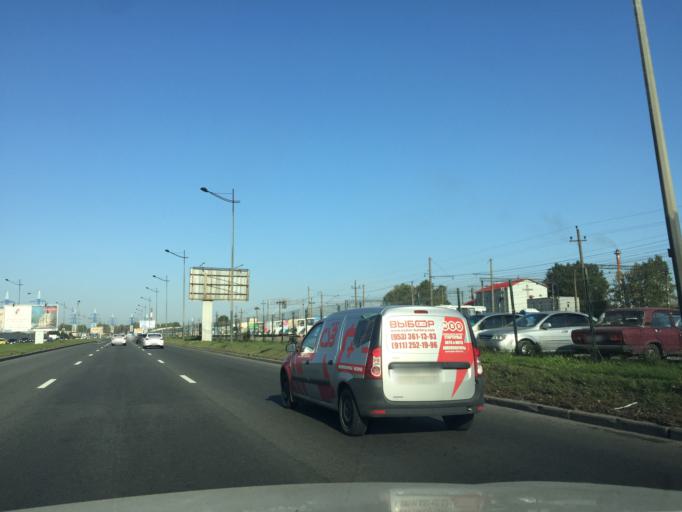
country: RU
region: St.-Petersburg
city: Kupchino
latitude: 59.8813
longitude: 30.3470
